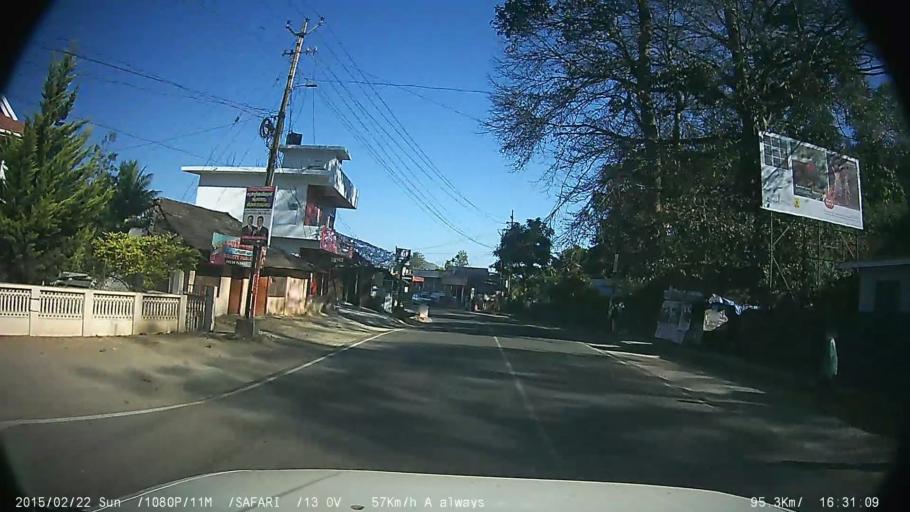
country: IN
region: Tamil Nadu
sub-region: Theni
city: Gudalur
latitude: 9.6074
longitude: 77.1624
